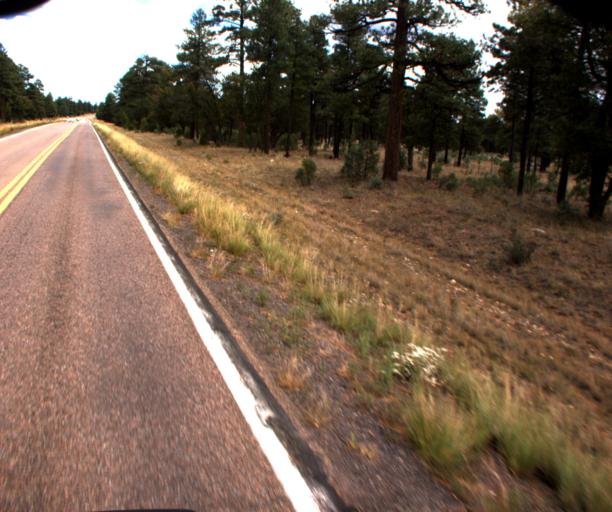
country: US
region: Arizona
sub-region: Navajo County
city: Heber-Overgaard
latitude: 34.4275
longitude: -110.6474
